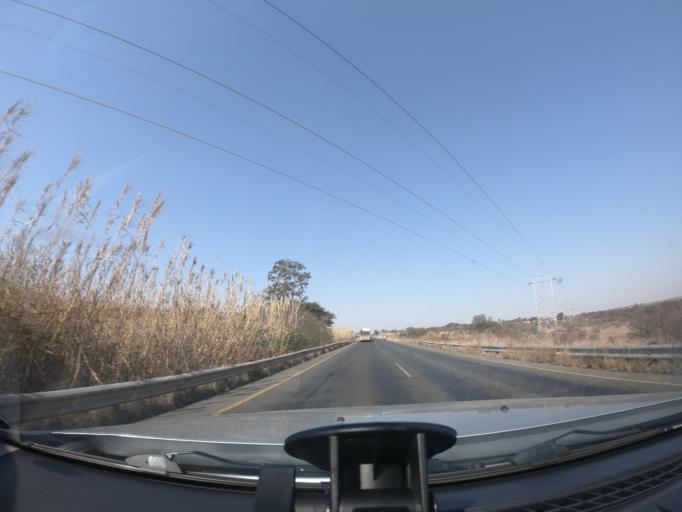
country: ZA
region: KwaZulu-Natal
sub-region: uThukela District Municipality
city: Ladysmith
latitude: -28.7454
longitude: 29.8203
